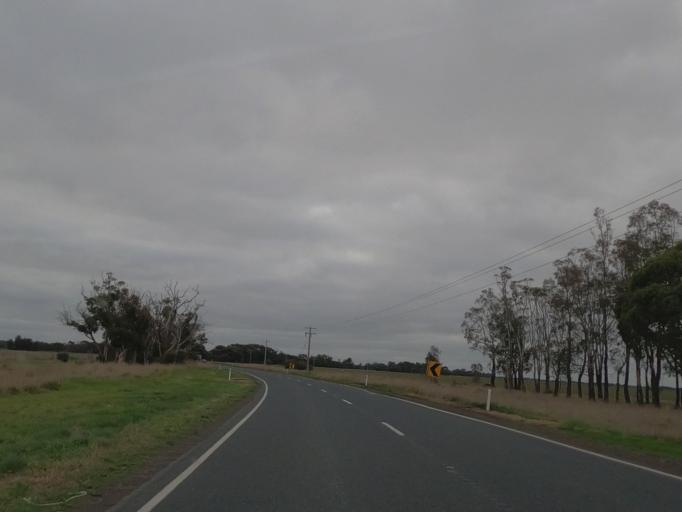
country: AU
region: Victoria
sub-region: Greater Bendigo
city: Long Gully
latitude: -36.3768
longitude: 143.9775
